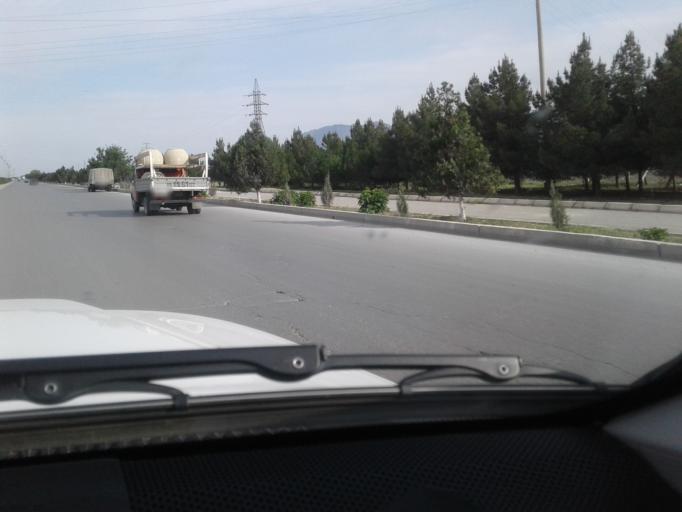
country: TM
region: Ahal
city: Abadan
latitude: 38.1541
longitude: 57.9762
